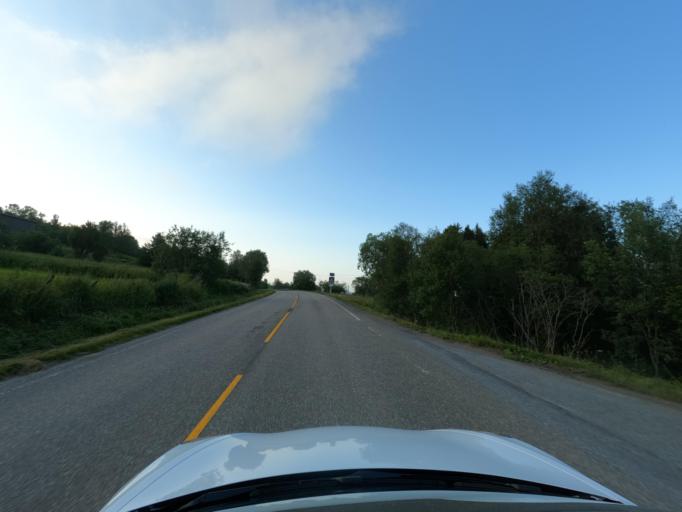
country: NO
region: Troms
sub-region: Skanland
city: Evenskjer
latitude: 68.6480
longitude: 16.5865
